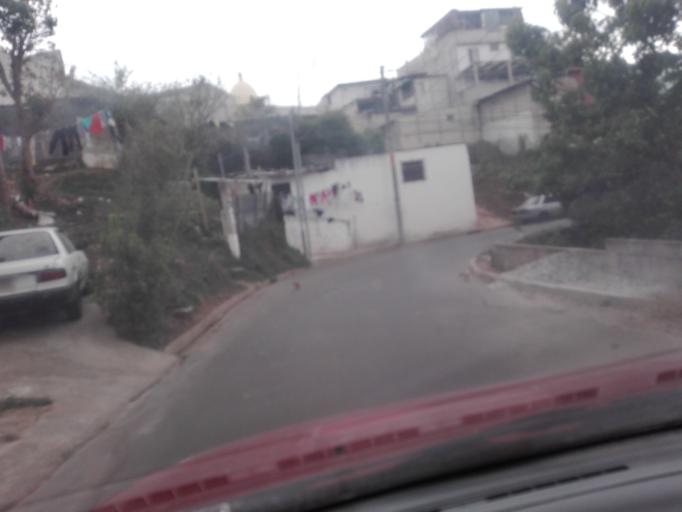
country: GT
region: Guatemala
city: San Jose Pinula
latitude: 14.5724
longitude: -90.4471
